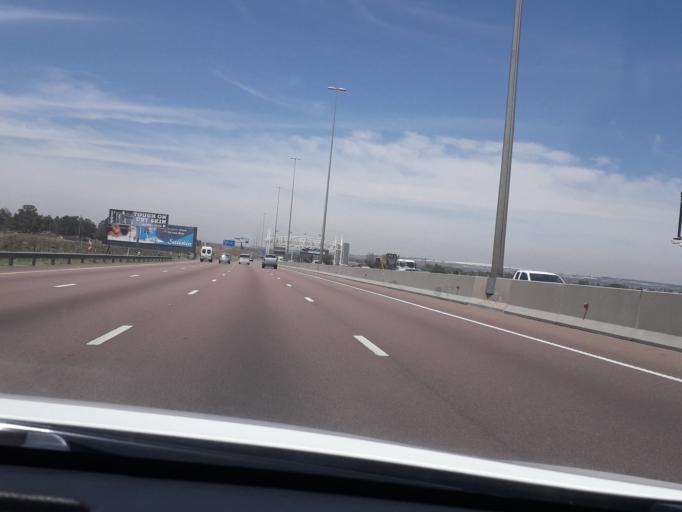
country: ZA
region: Gauteng
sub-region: City of Tshwane Metropolitan Municipality
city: Centurion
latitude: -25.8458
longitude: 28.2299
